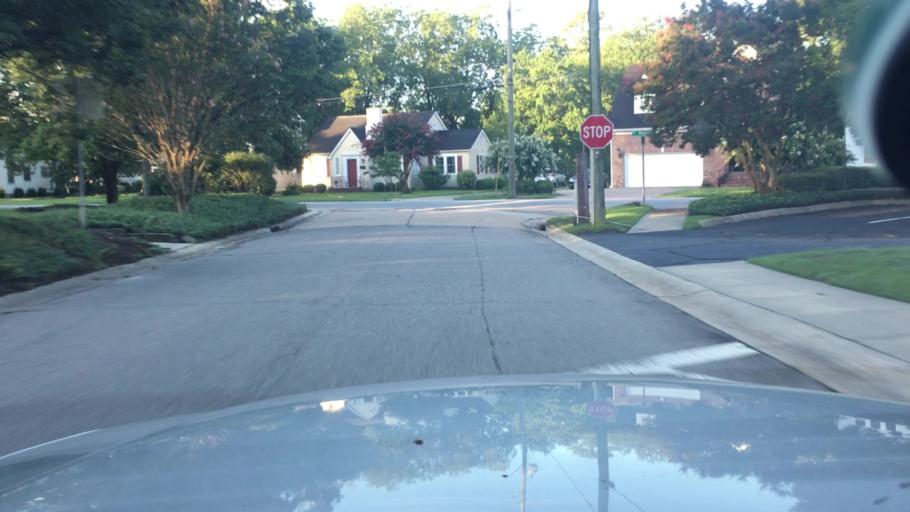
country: US
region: North Carolina
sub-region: Cumberland County
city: Fayetteville
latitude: 35.0626
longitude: -78.9087
